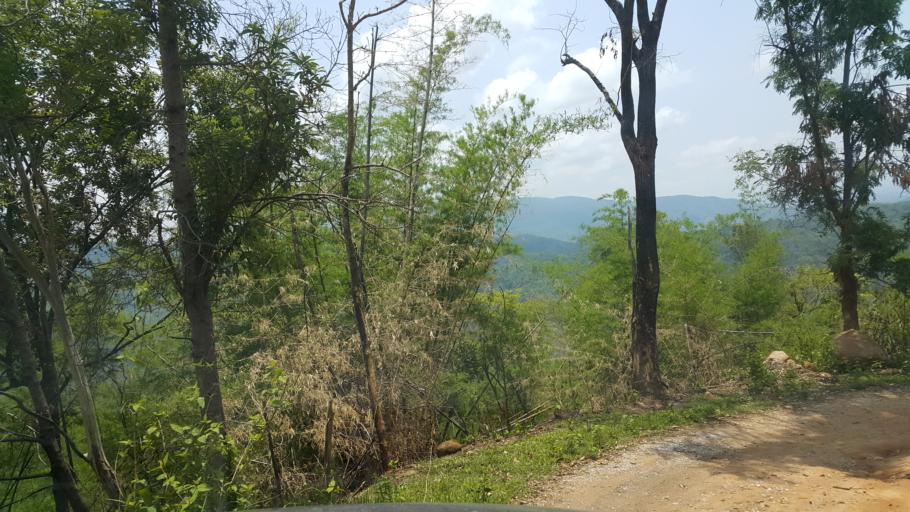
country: TH
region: Chiang Rai
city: Chiang Rai
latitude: 19.9989
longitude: 99.7093
